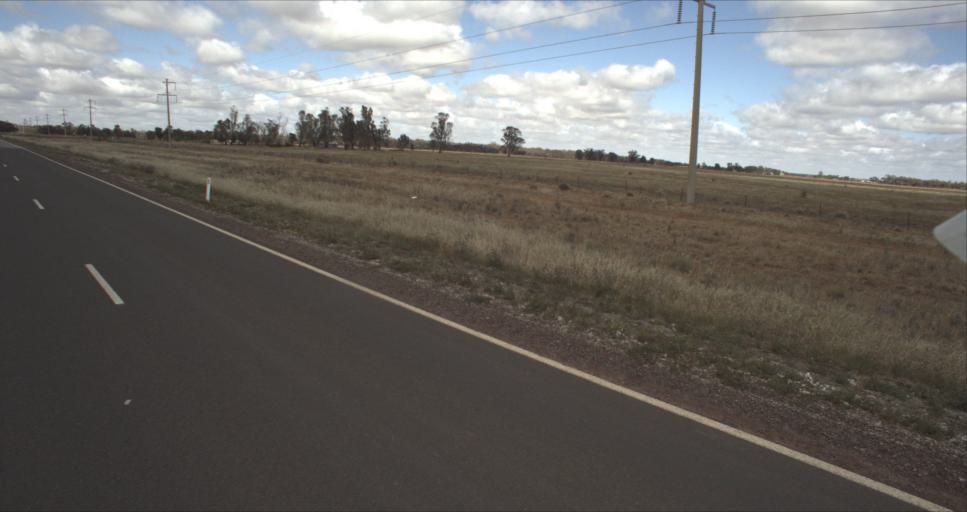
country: AU
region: New South Wales
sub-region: Murrumbidgee Shire
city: Darlington Point
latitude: -34.5893
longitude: 146.1638
